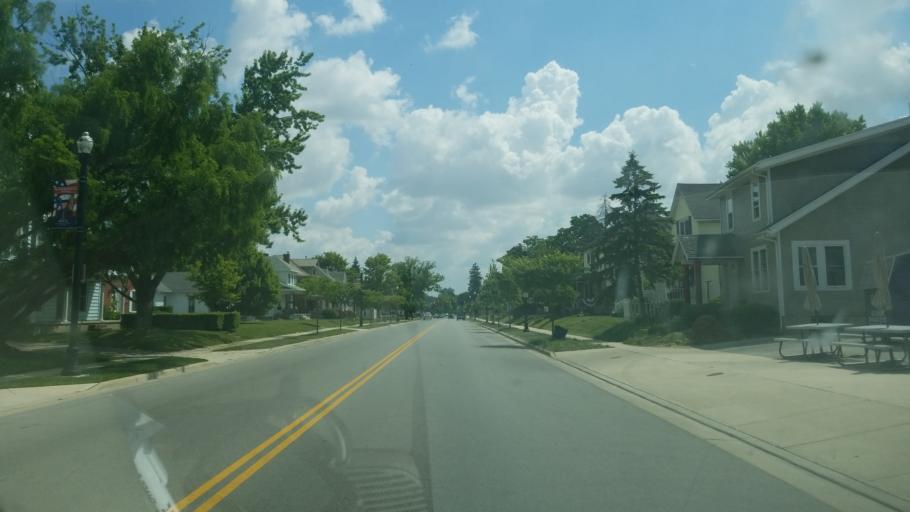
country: US
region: Ohio
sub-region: Auglaize County
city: Wapakoneta
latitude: 40.5684
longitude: -84.2054
